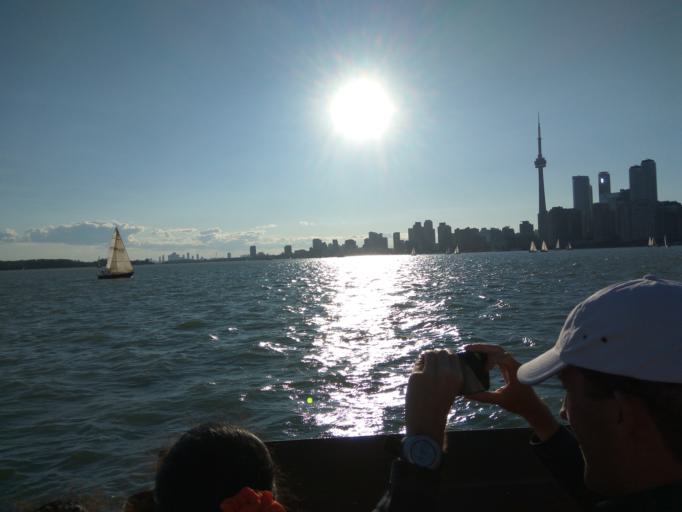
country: CA
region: Ontario
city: Toronto
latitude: 43.6314
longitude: -79.3631
